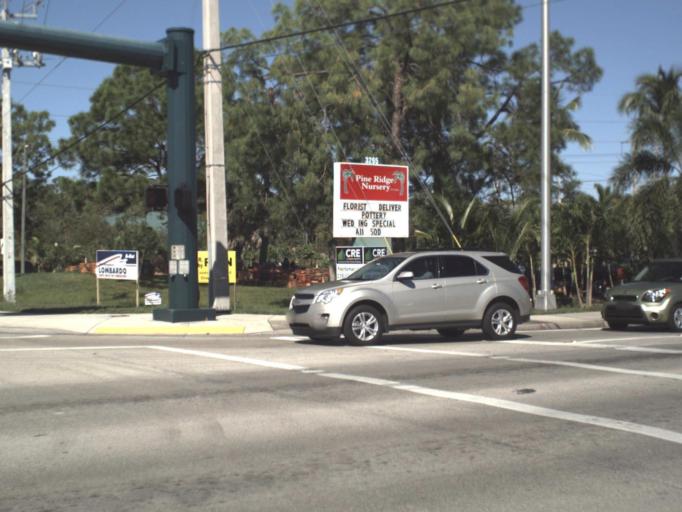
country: US
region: Florida
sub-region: Collier County
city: Vineyards
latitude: 26.2118
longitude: -81.7515
